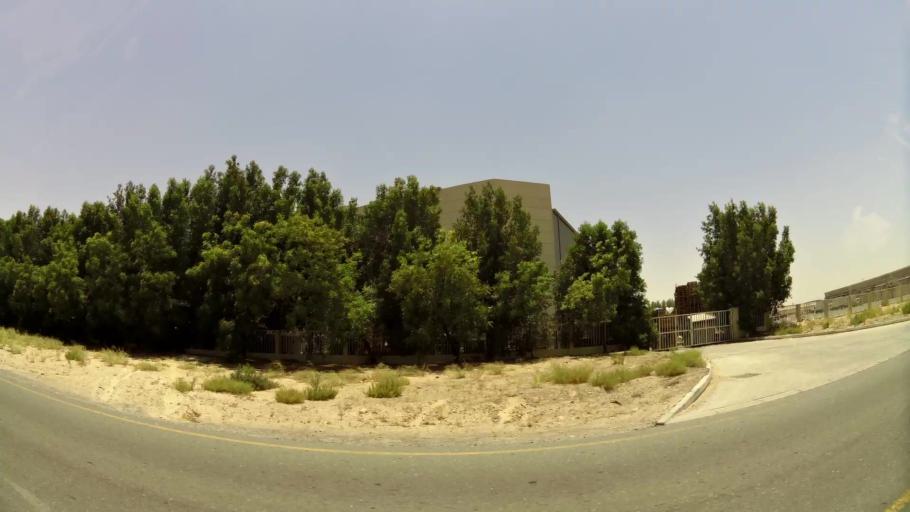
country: AE
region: Dubai
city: Dubai
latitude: 24.9842
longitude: 55.1694
